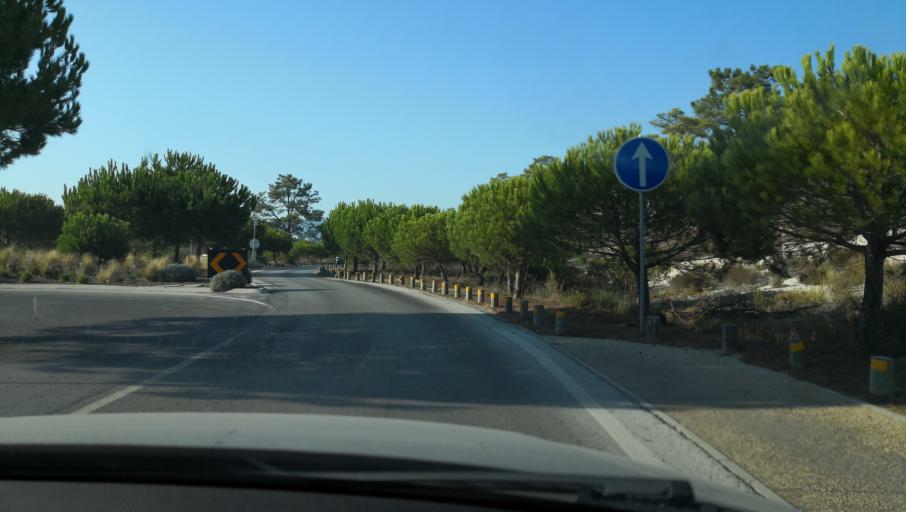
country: PT
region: Setubal
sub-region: Setubal
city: Setubal
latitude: 38.4757
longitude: -8.8866
